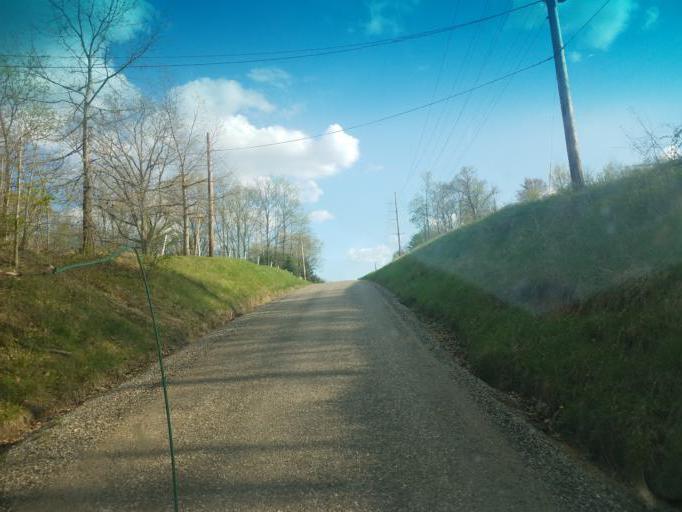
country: US
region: Ohio
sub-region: Wayne County
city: Shreve
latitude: 40.6483
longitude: -82.0336
